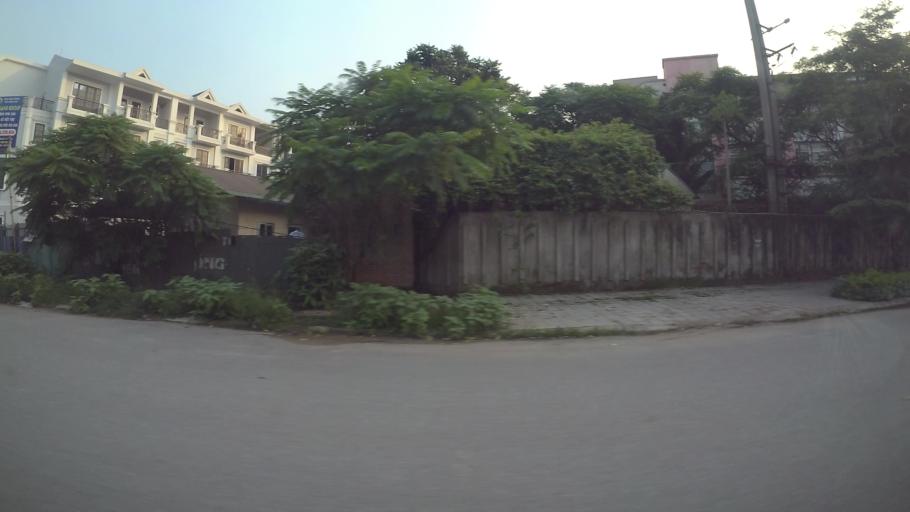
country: VN
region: Ha Noi
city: Thanh Xuan
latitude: 20.9766
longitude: 105.8166
